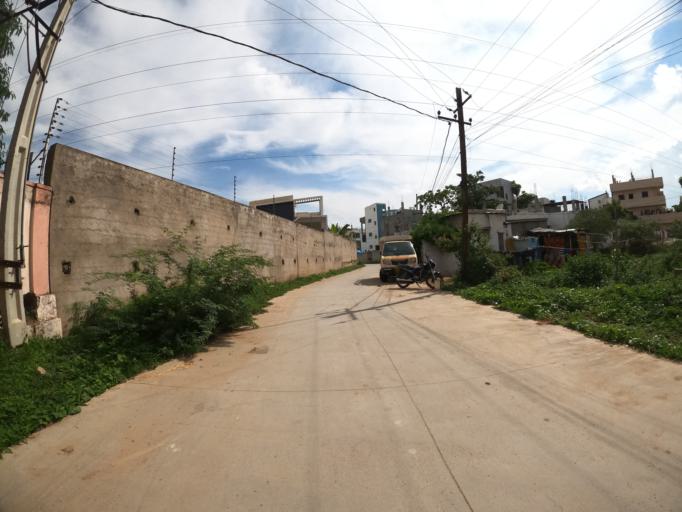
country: IN
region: Telangana
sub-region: Hyderabad
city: Hyderabad
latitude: 17.3604
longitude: 78.3797
